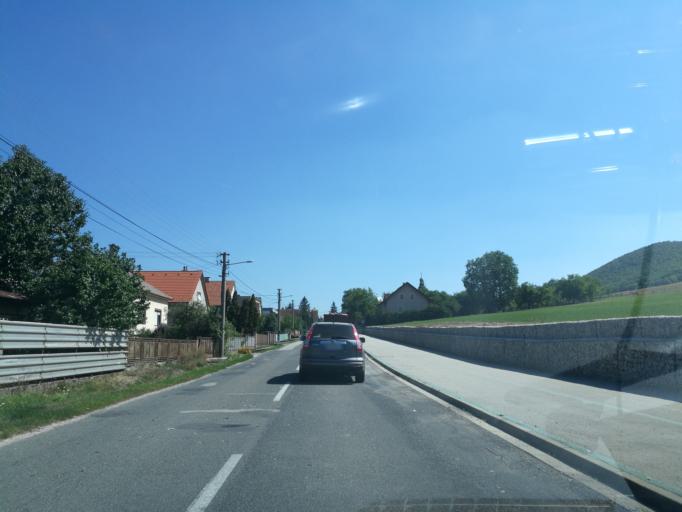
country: SK
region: Nitriansky
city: Brezova pod Bradlom
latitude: 48.6716
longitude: 17.5919
